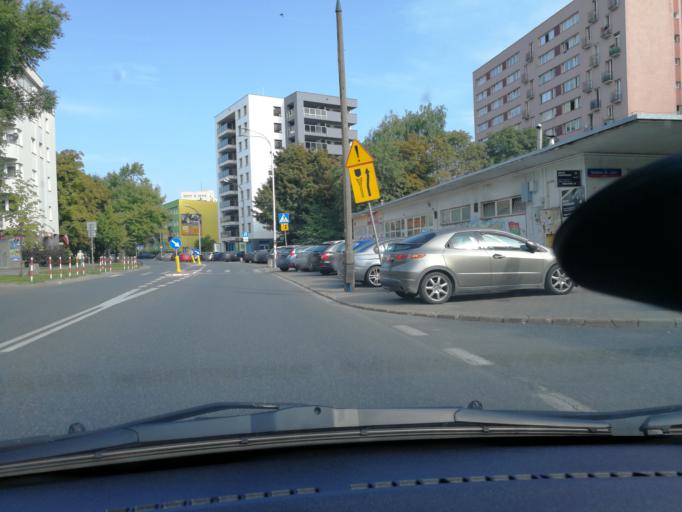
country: PL
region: Masovian Voivodeship
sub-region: Warszawa
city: Bemowo
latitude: 52.2341
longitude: 20.9409
